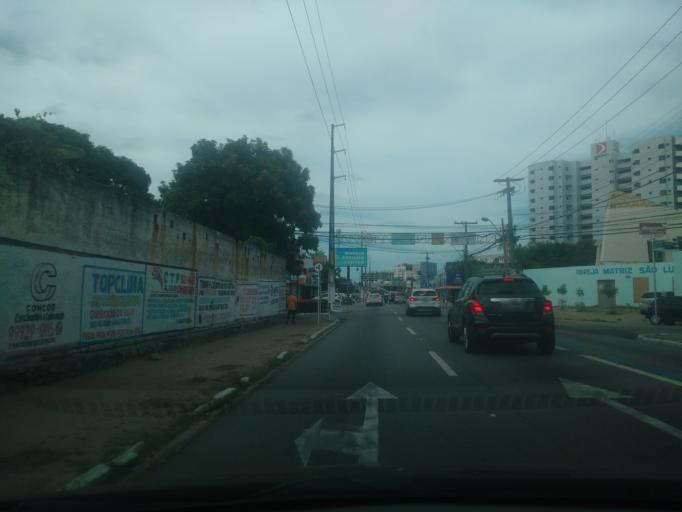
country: BR
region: Alagoas
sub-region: Maceio
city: Maceio
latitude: -9.6471
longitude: -35.7124
